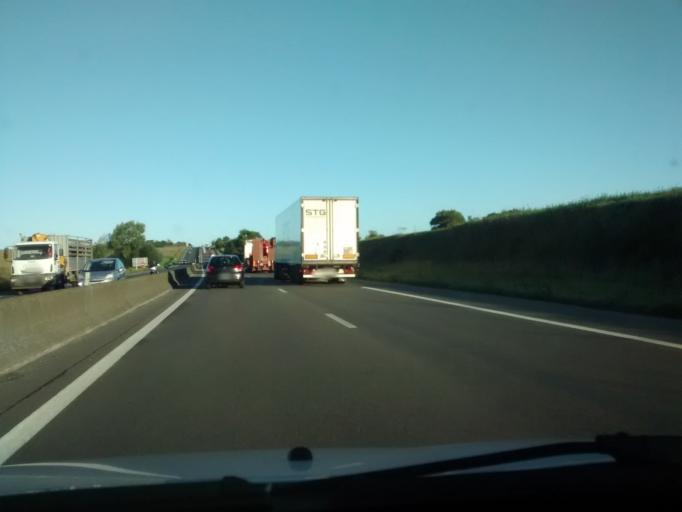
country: FR
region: Brittany
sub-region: Departement d'Ille-et-Vilaine
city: Saint-Pere
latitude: 48.5717
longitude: -1.9342
